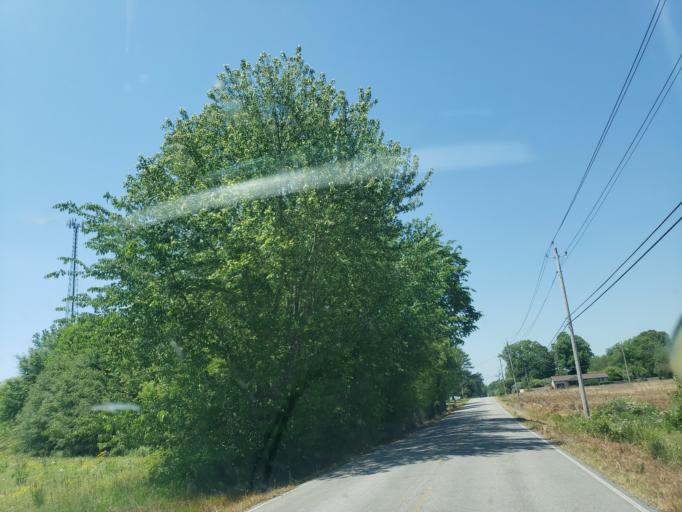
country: US
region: Alabama
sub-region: Madison County
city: Harvest
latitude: 34.9623
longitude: -86.7018
